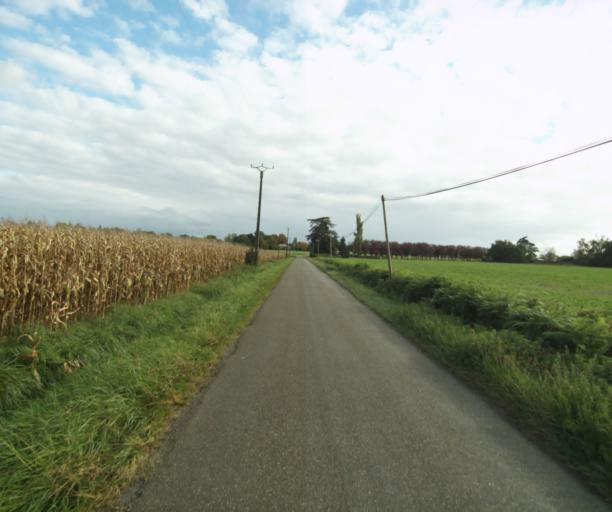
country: FR
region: Midi-Pyrenees
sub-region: Departement du Gers
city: Eauze
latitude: 43.8715
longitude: 0.0908
